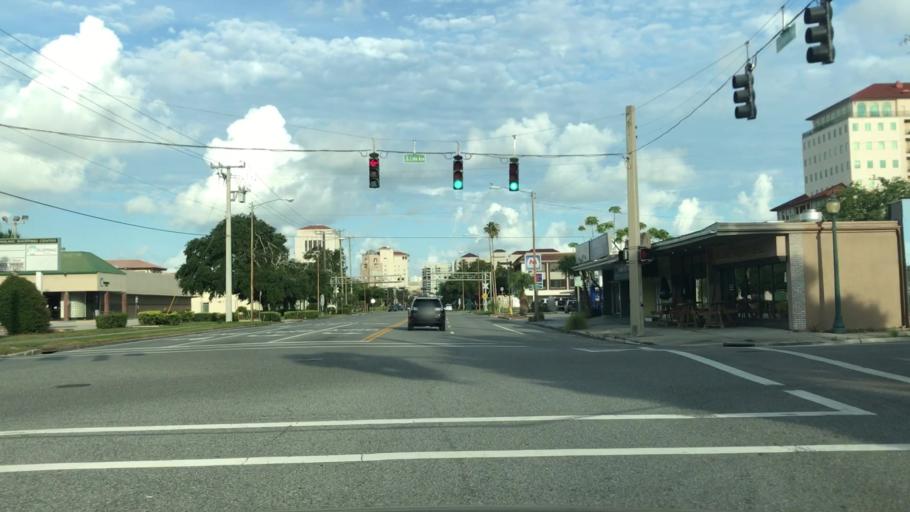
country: US
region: Florida
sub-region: Sarasota County
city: Sarasota
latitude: 27.3357
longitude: -82.5240
